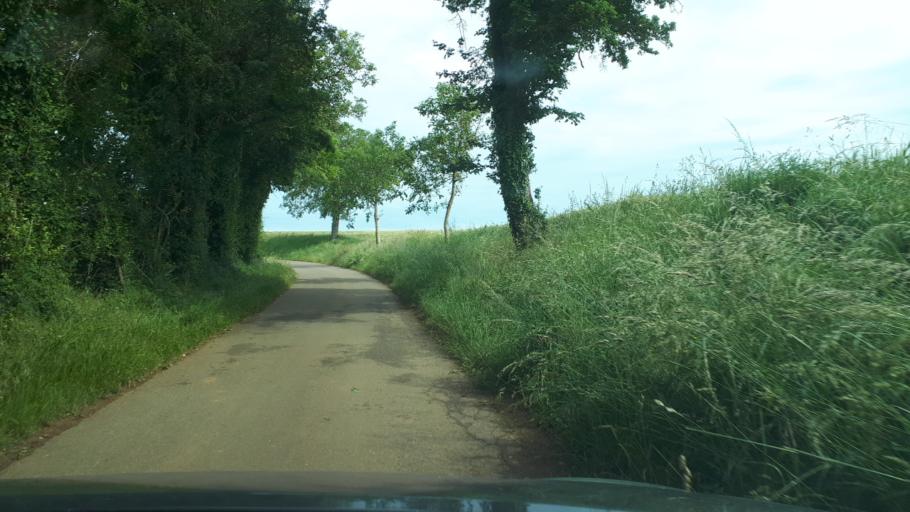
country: FR
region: Centre
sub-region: Departement du Cher
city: Sancerre
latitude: 47.3255
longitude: 2.7194
